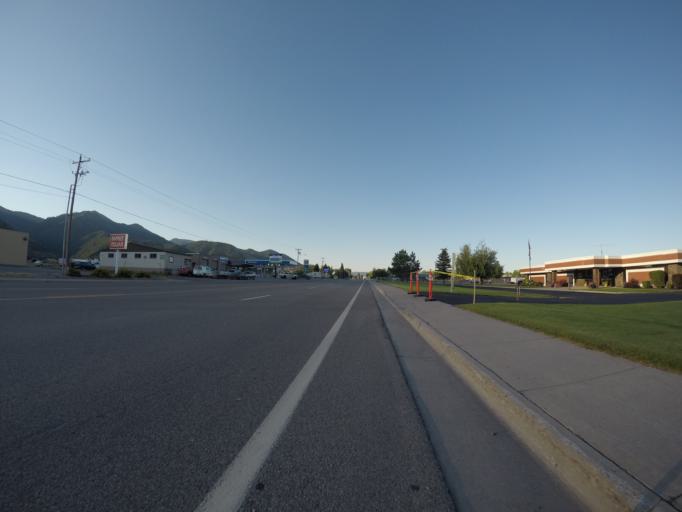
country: US
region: Wyoming
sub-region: Lincoln County
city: Afton
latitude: 42.7368
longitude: -110.9334
